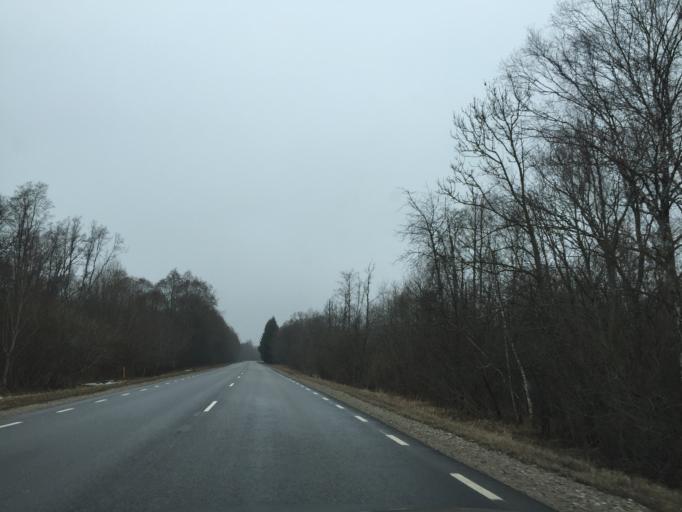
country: EE
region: Laeaene
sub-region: Lihula vald
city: Lihula
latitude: 58.5927
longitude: 23.7099
